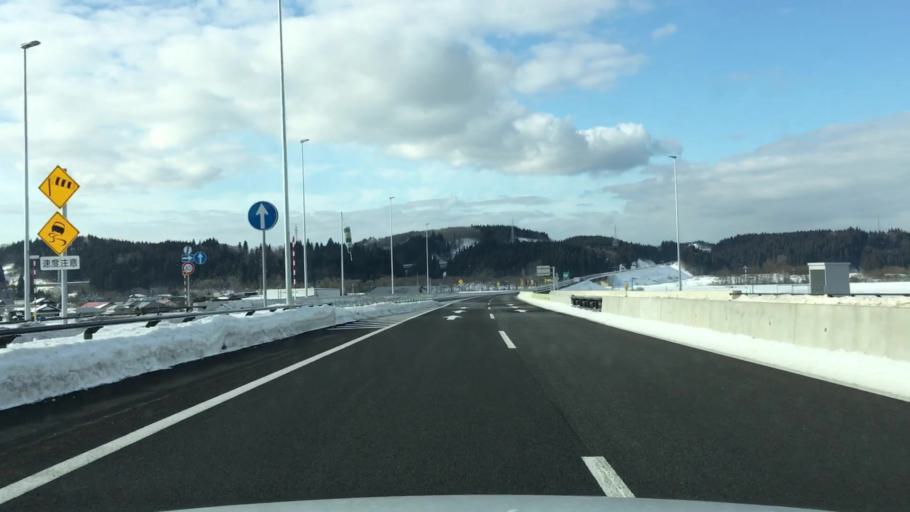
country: JP
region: Akita
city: Takanosu
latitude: 40.2010
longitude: 140.3936
